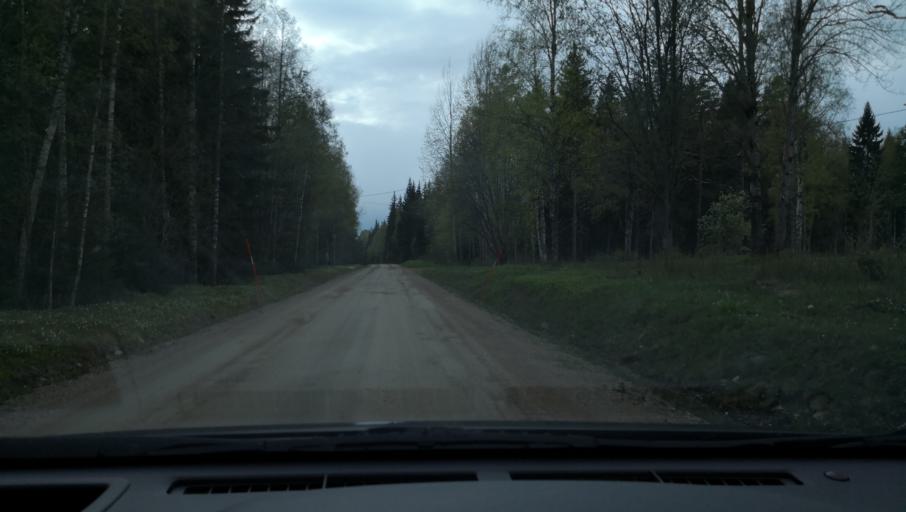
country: SE
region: Vaestmanland
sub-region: Fagersta Kommun
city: Fagersta
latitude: 60.1211
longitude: 15.6969
